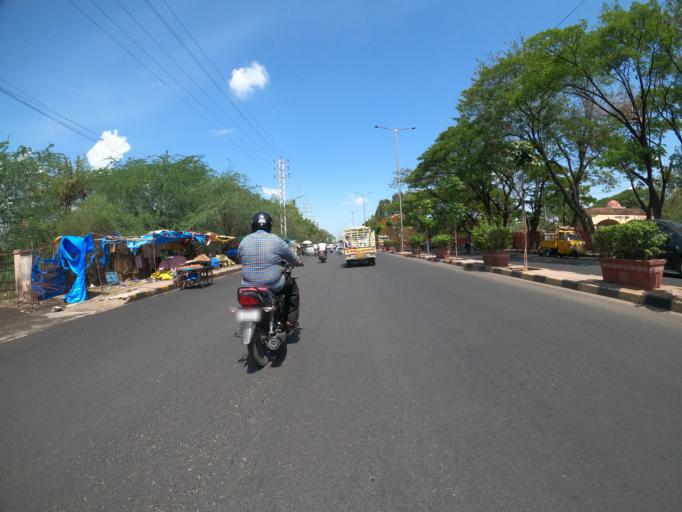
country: IN
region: Telangana
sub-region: Hyderabad
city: Hyderabad
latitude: 17.3731
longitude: 78.4096
